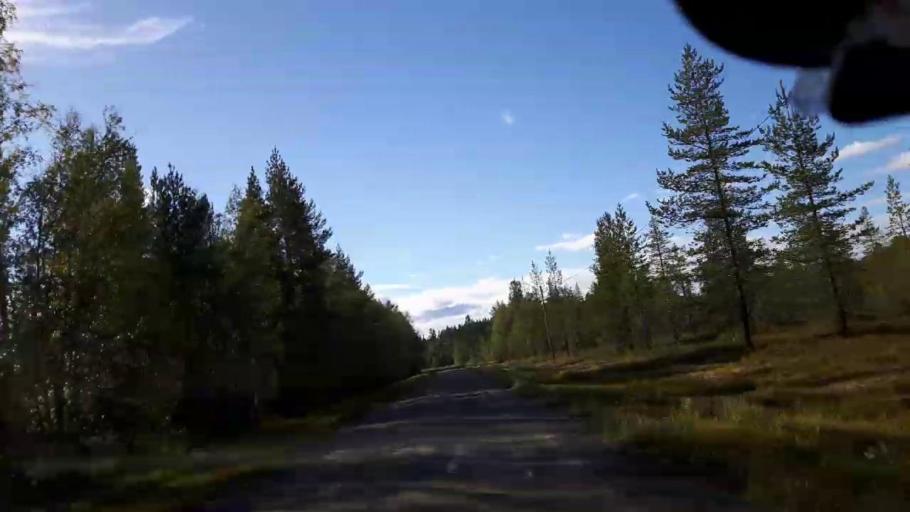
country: SE
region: Jaemtland
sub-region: Ragunda Kommun
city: Hammarstrand
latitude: 63.4805
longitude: 16.1338
